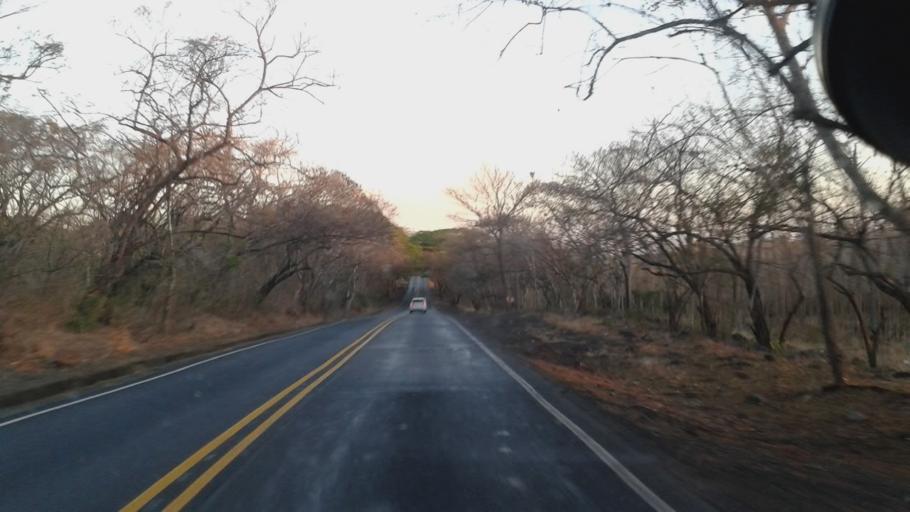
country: CR
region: Guanacaste
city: Juntas
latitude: 10.1493
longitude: -84.9117
